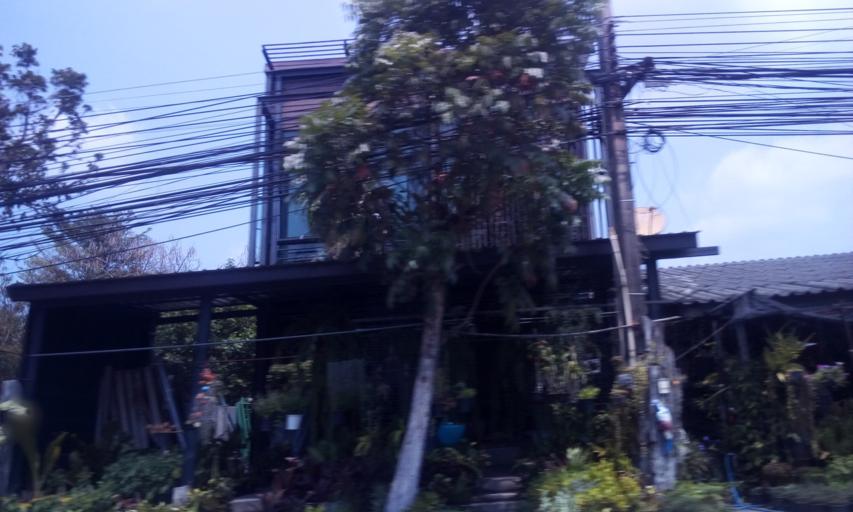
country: TH
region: Chachoengsao
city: Chachoengsao
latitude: 13.6711
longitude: 101.0848
